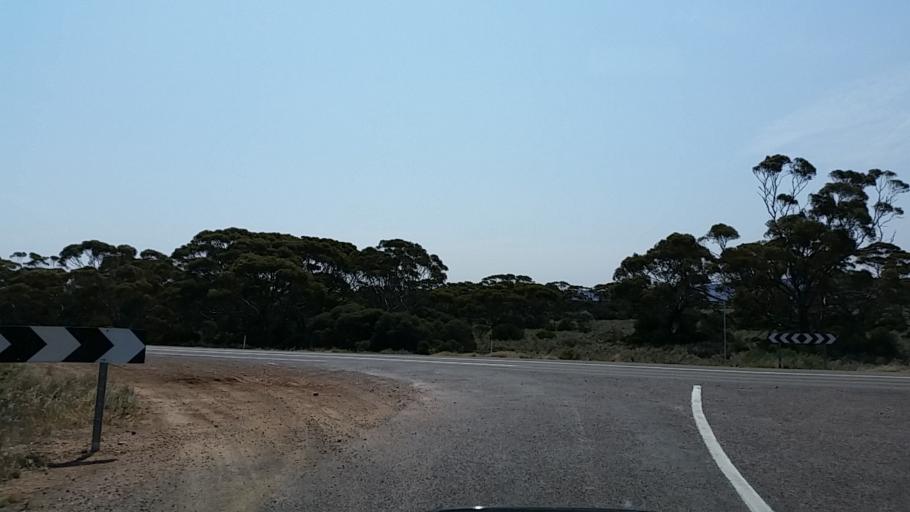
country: AU
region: South Australia
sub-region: Port Pirie City and Dists
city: Port Pirie
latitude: -32.9909
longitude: 137.9896
